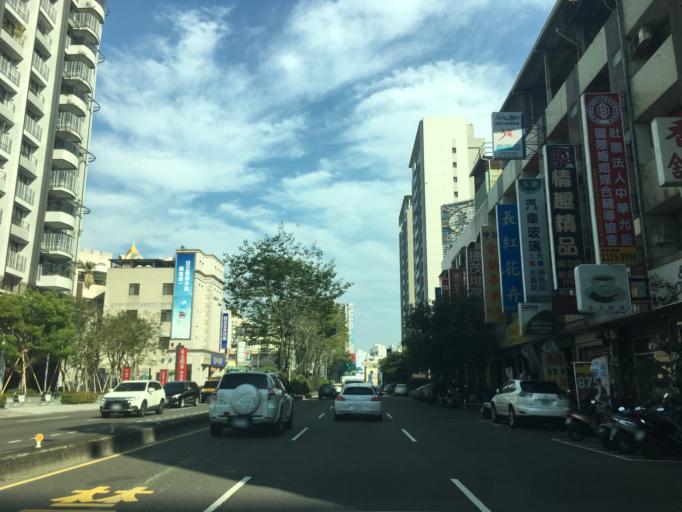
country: TW
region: Taiwan
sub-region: Taichung City
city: Taichung
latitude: 24.1441
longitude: 120.6344
